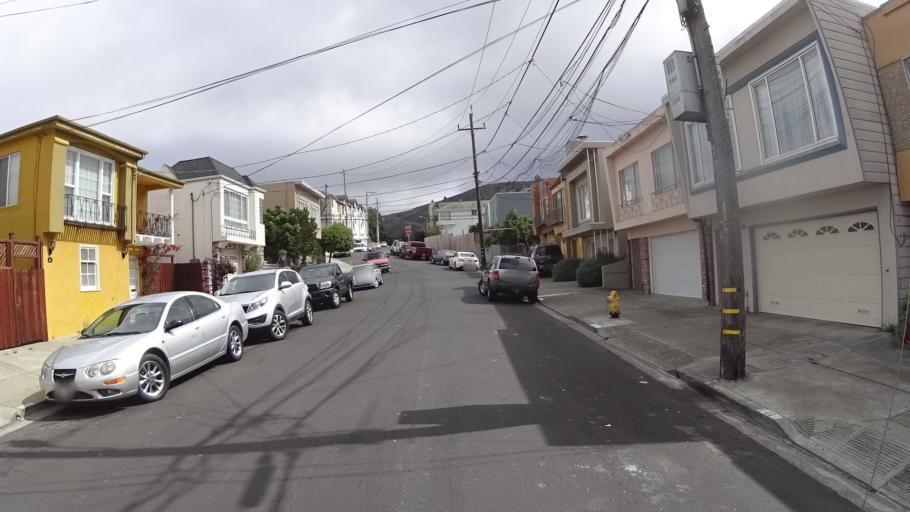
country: US
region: California
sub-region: San Mateo County
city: Daly City
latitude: 37.6944
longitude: -122.4629
